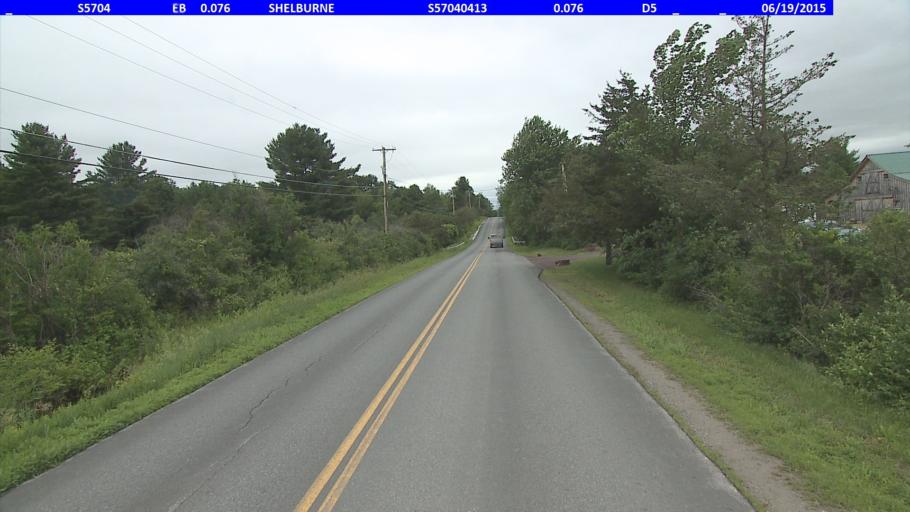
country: US
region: Vermont
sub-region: Chittenden County
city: Burlington
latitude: 44.3959
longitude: -73.2453
